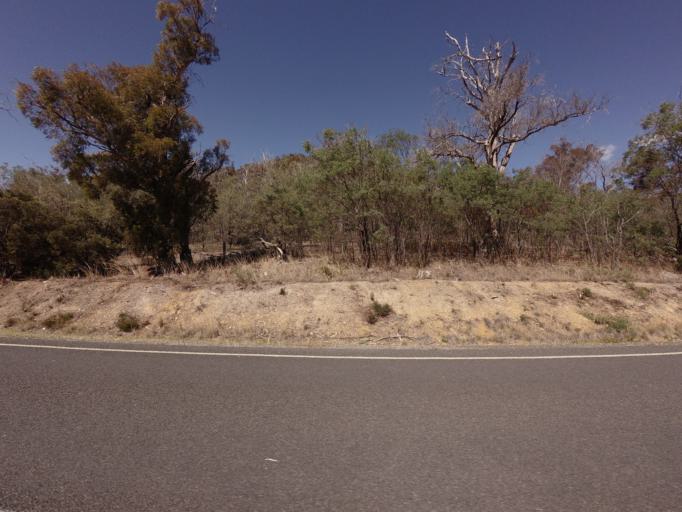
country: AU
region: Tasmania
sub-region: Break O'Day
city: St Helens
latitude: -41.6858
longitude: 147.8817
